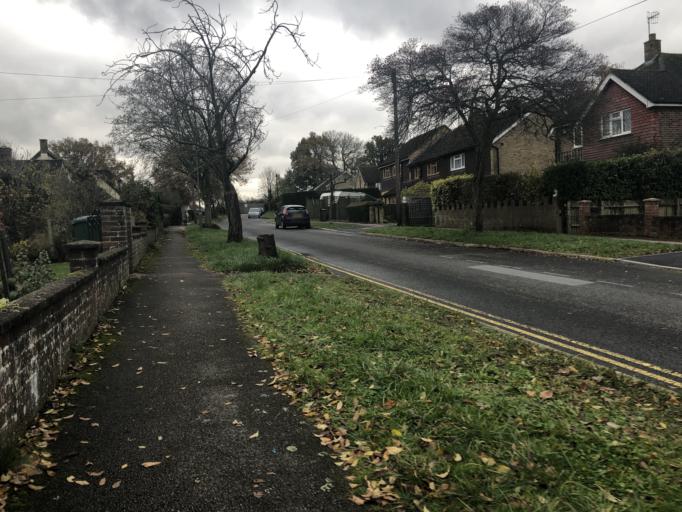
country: GB
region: England
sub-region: Surrey
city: Salfords
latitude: 51.2031
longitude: -0.1633
